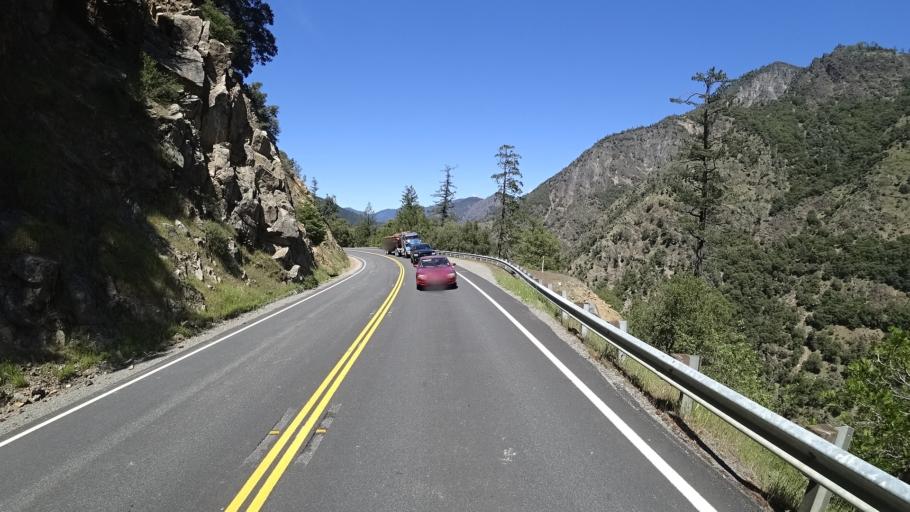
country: US
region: California
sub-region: Humboldt County
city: Willow Creek
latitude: 40.8167
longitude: -123.4785
